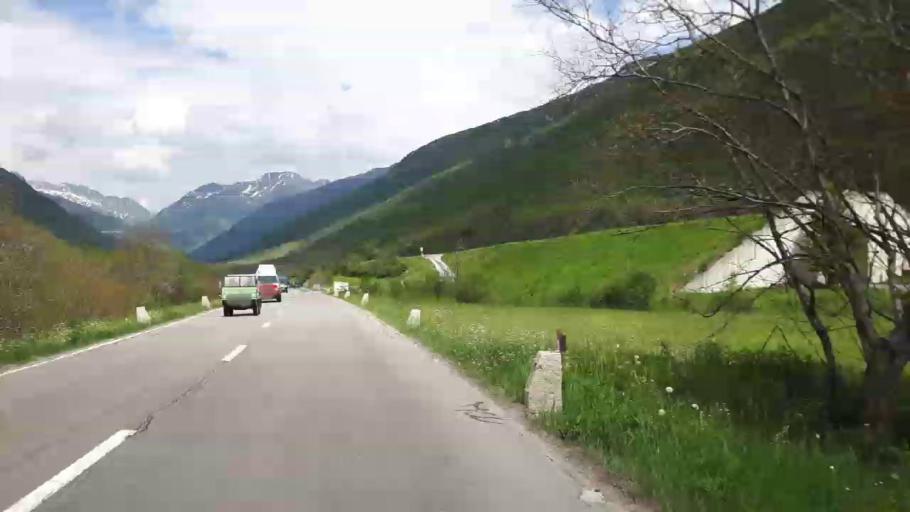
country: CH
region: Uri
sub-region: Uri
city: Andermatt
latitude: 46.6011
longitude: 8.5089
